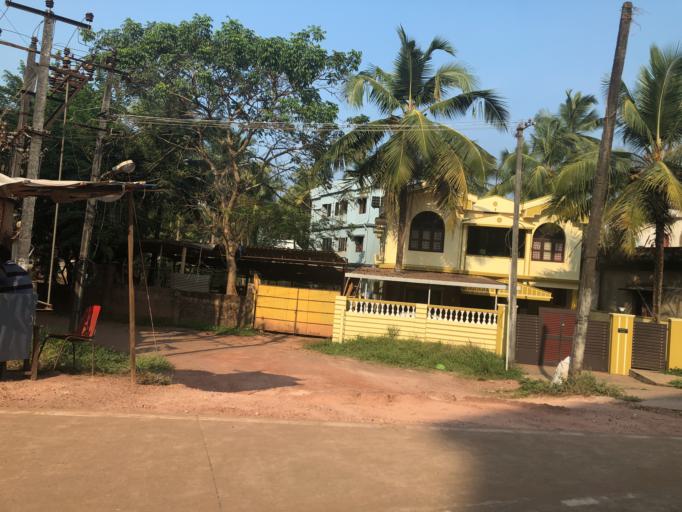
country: IN
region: Karnataka
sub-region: Dakshina Kannada
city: Ullal
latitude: 12.8168
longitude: 74.8467
